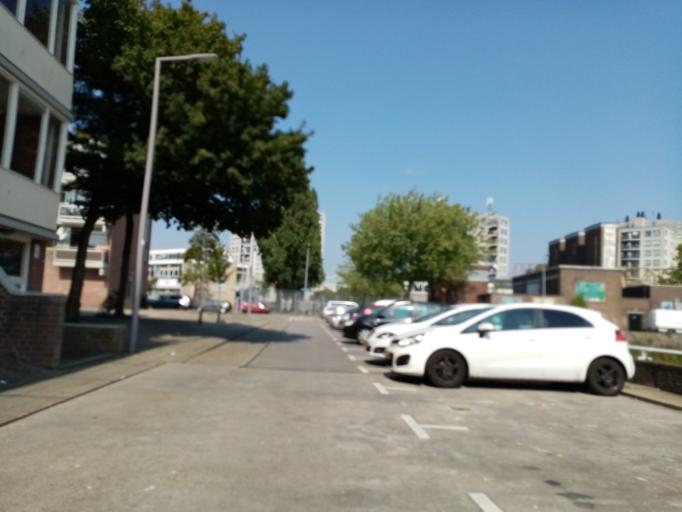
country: NL
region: South Holland
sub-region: Gemeente Rotterdam
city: Rotterdam
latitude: 51.9089
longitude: 4.5091
